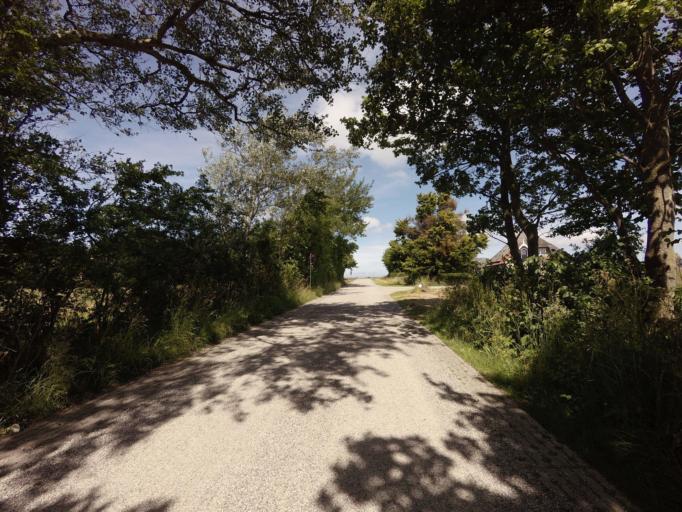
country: NL
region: North Holland
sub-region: Gemeente Texel
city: Den Burg
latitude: 53.0654
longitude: 4.8072
